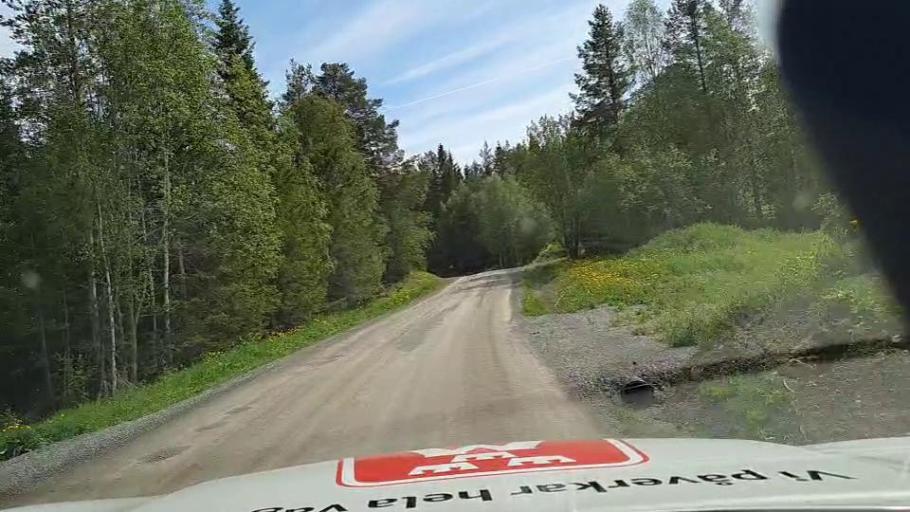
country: SE
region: Jaemtland
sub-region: OEstersunds Kommun
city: Brunflo
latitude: 63.0109
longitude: 14.7826
